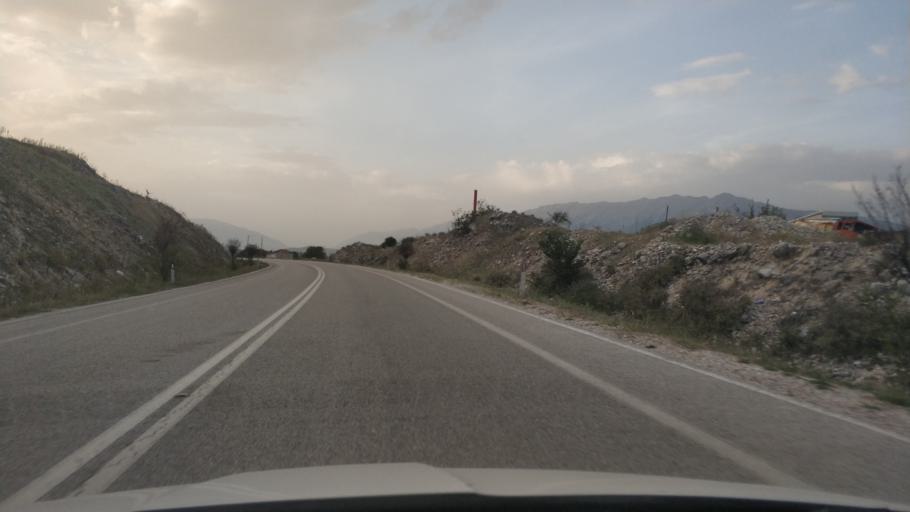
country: AL
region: Gjirokaster
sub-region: Rrethi i Gjirokastres
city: Libohove
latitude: 39.9744
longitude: 20.2354
